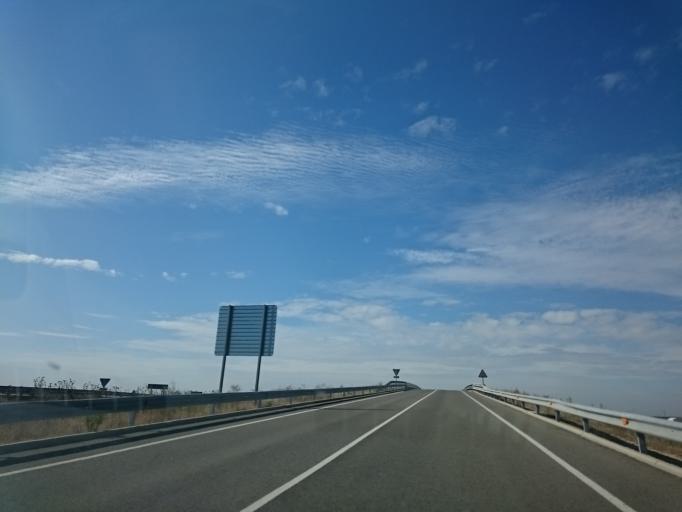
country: ES
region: Catalonia
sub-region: Provincia de Lleida
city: Alguaire
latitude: 41.7329
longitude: 0.5614
